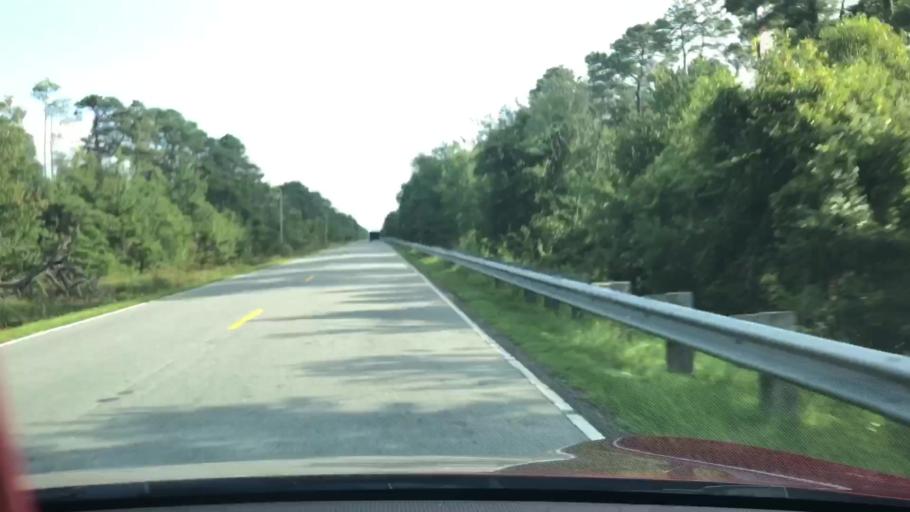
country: US
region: North Carolina
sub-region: Dare County
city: Wanchese
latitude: 35.7362
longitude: -75.7687
